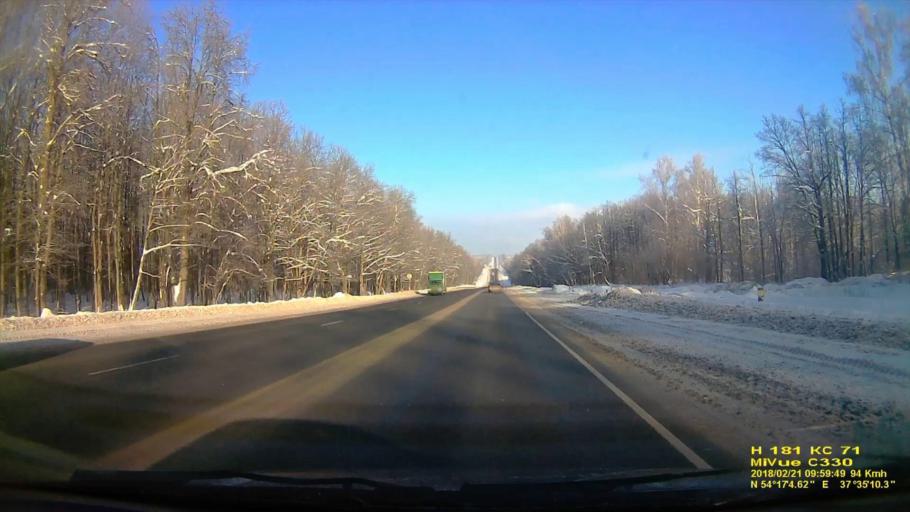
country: RU
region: Tula
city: Gorelki
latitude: 54.2848
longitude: 37.5861
